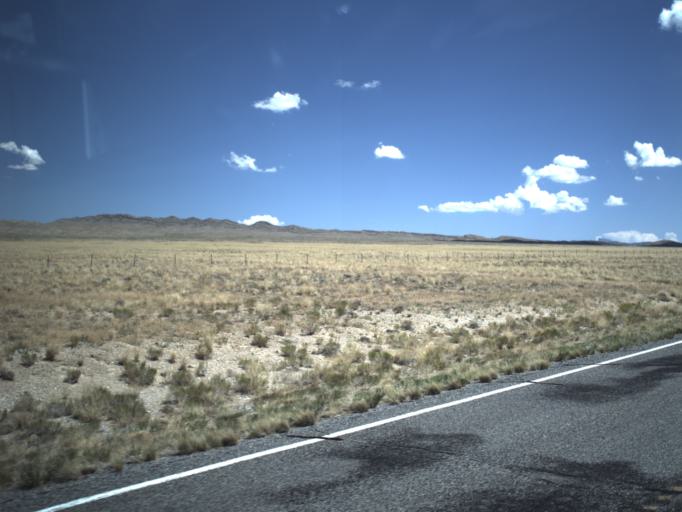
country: US
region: Nevada
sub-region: White Pine County
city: McGill
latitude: 39.0433
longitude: -113.8688
